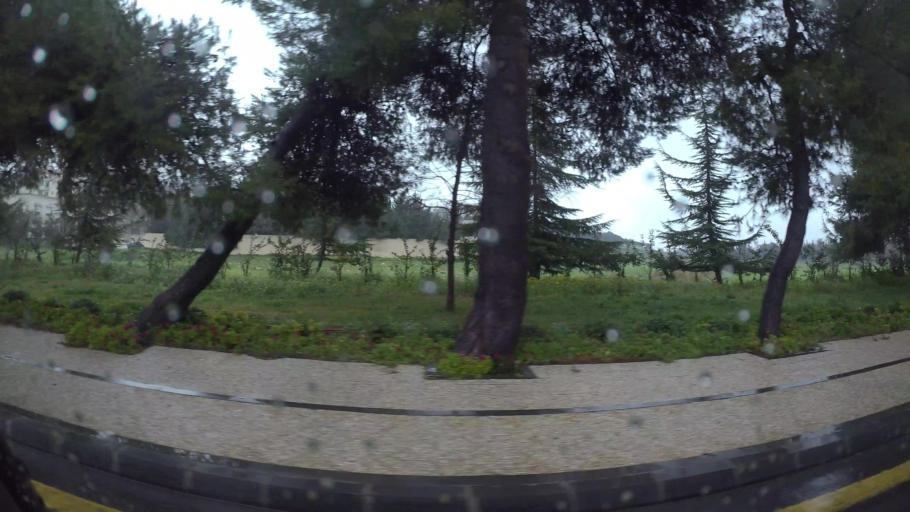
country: JO
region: Amman
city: Wadi as Sir
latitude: 31.9958
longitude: 35.8173
